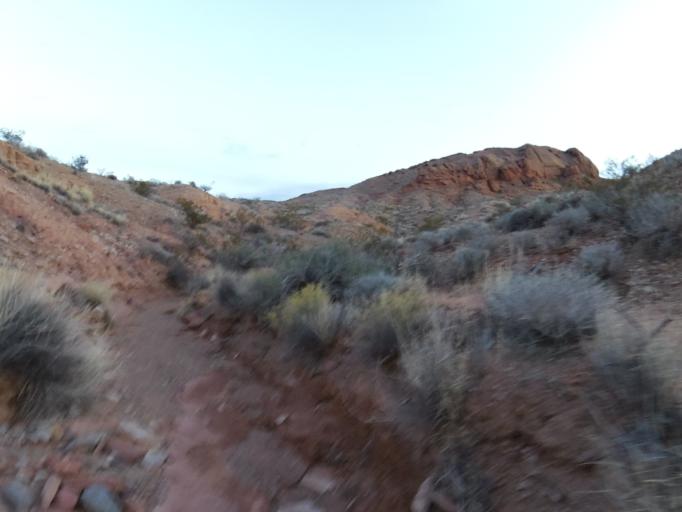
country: US
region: Nevada
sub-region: Clark County
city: Boulder City
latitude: 36.2386
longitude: -114.6277
